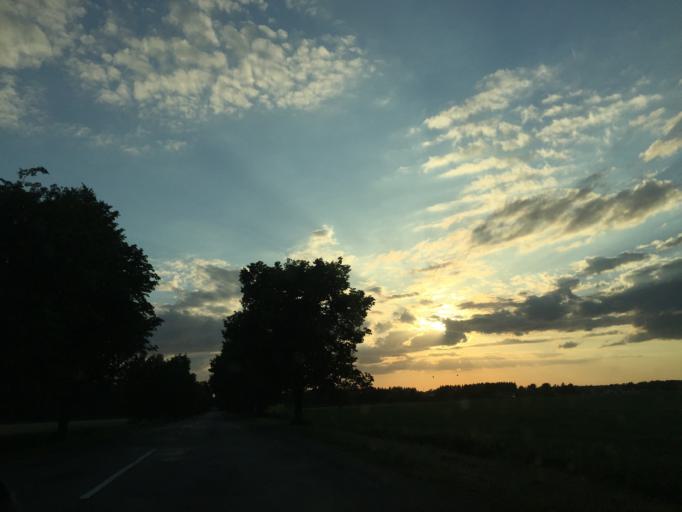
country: LV
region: Sigulda
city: Sigulda
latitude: 57.1377
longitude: 24.8904
